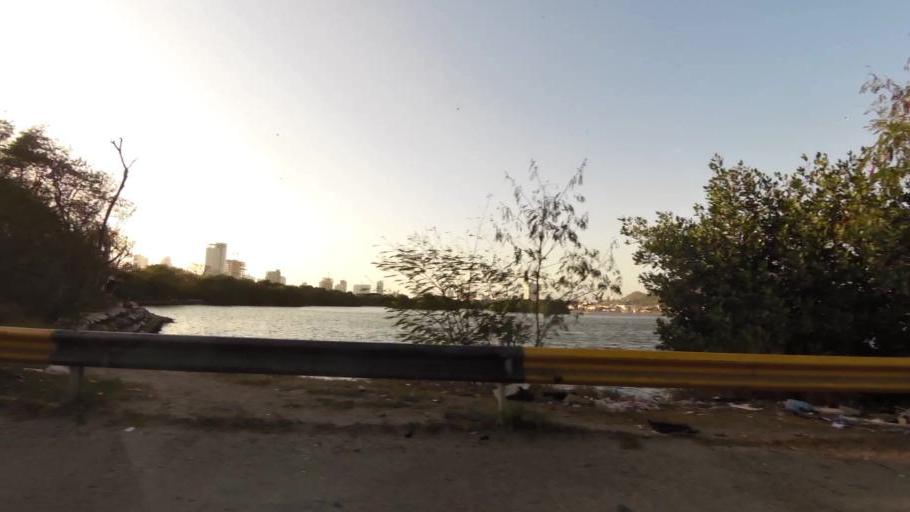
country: CO
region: Bolivar
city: Cartagena
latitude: 10.4058
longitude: -75.5242
